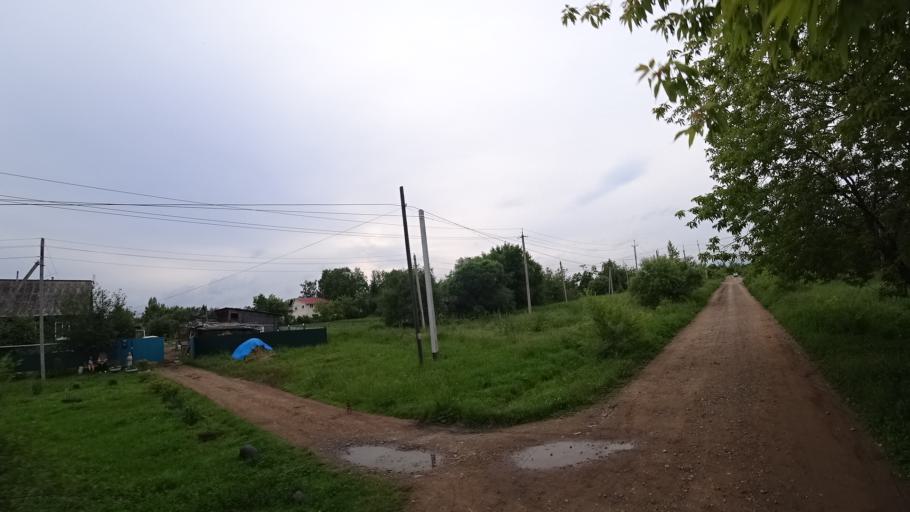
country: RU
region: Primorskiy
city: Novosysoyevka
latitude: 44.2324
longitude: 133.3655
